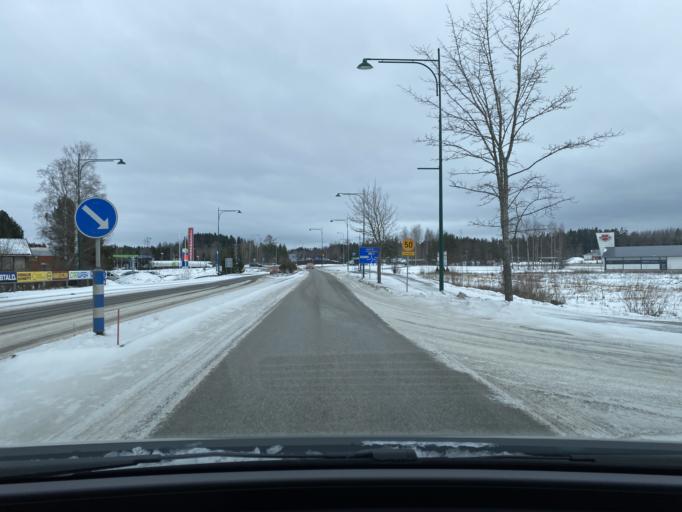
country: FI
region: Pirkanmaa
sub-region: Lounais-Pirkanmaa
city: Vammala
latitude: 61.3241
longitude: 22.9196
